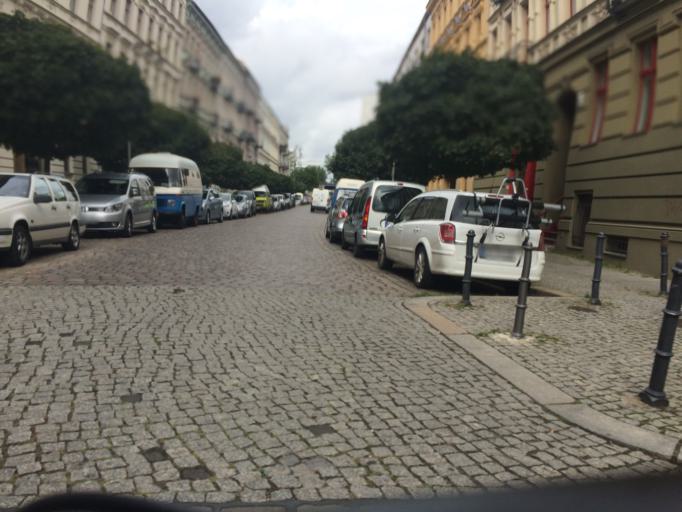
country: DE
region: Berlin
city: Rummelsburg
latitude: 52.5053
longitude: 13.4771
